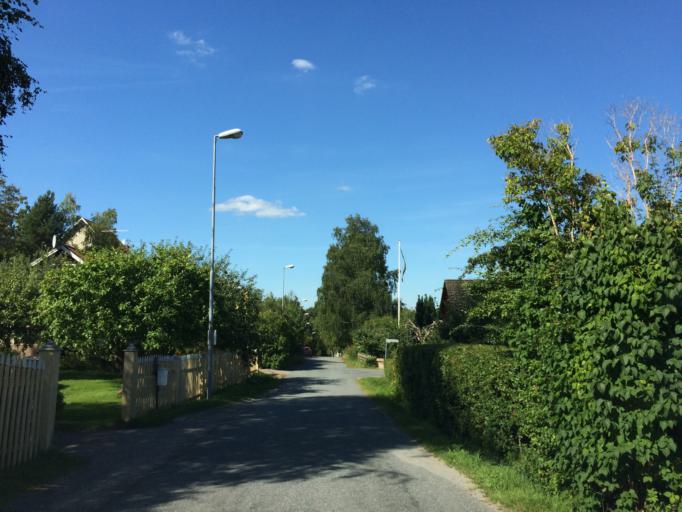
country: SE
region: Stockholm
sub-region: Sollentuna Kommun
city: Sollentuna
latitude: 59.4537
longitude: 17.9116
